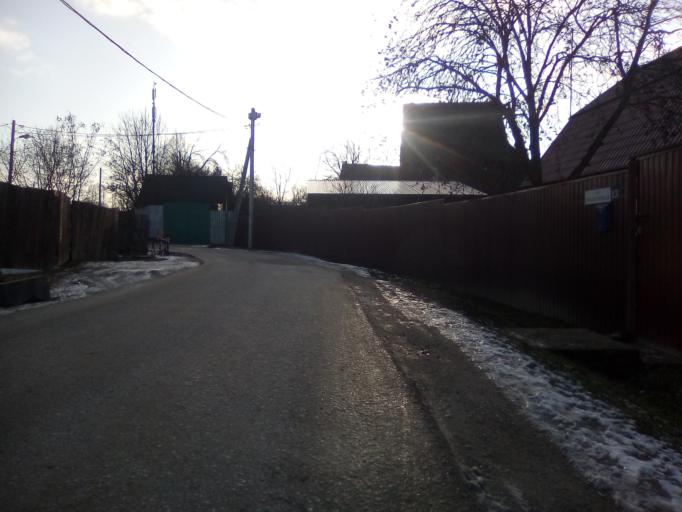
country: RU
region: Moskovskaya
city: Lesnoy Gorodok
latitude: 55.6690
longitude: 37.1787
